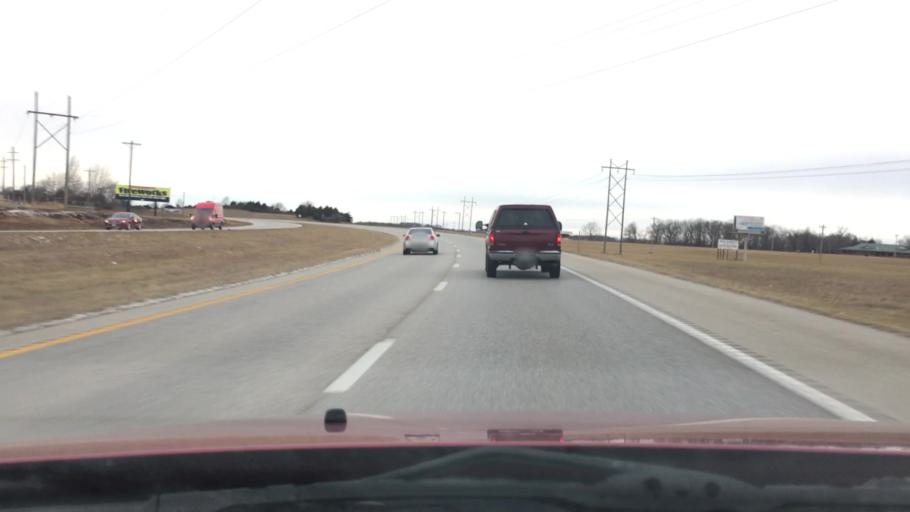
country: US
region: Missouri
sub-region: Webster County
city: Seymour
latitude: 37.1553
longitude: -92.7595
